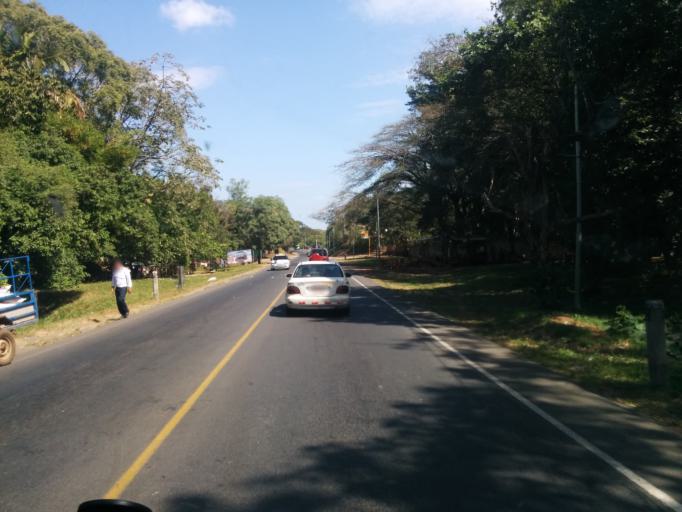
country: NI
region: Masaya
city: Masaya
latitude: 11.9582
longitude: -86.0894
